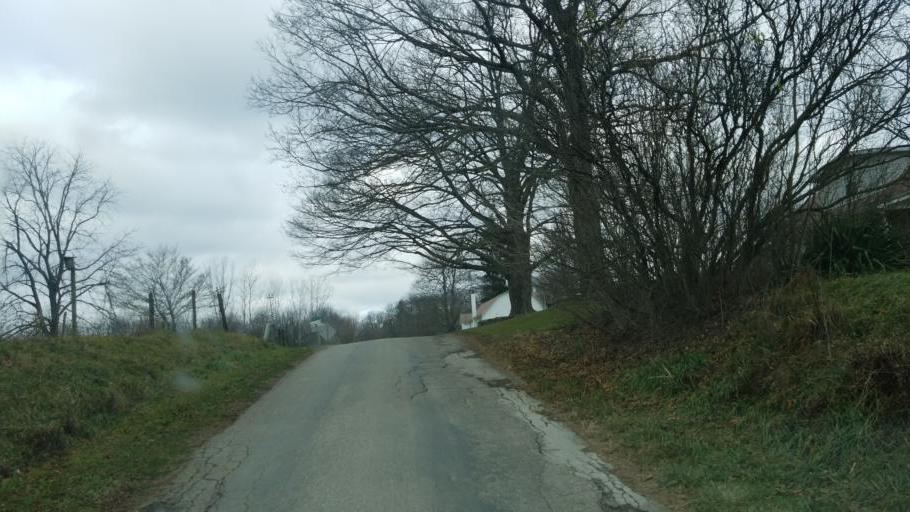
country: US
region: Ohio
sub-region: Richland County
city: Lexington
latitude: 40.6385
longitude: -82.6666
